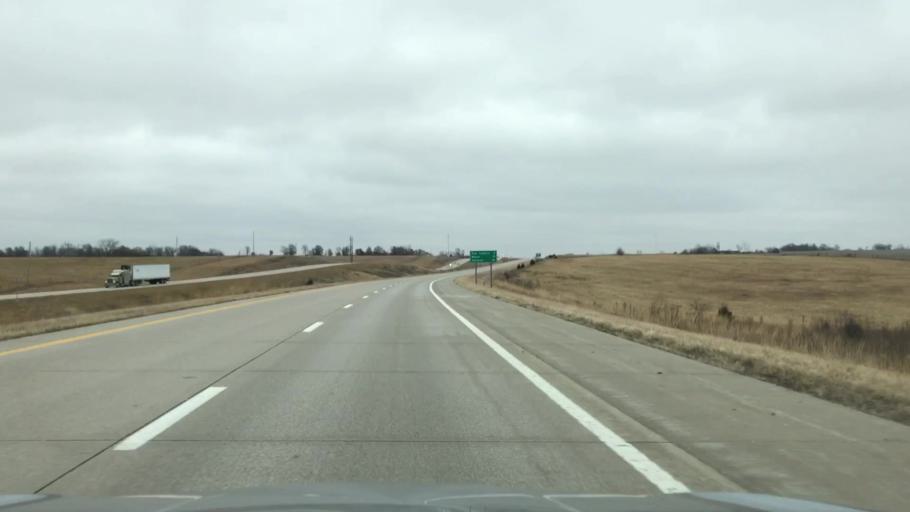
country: US
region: Missouri
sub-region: Linn County
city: Marceline
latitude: 39.7645
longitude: -92.7873
